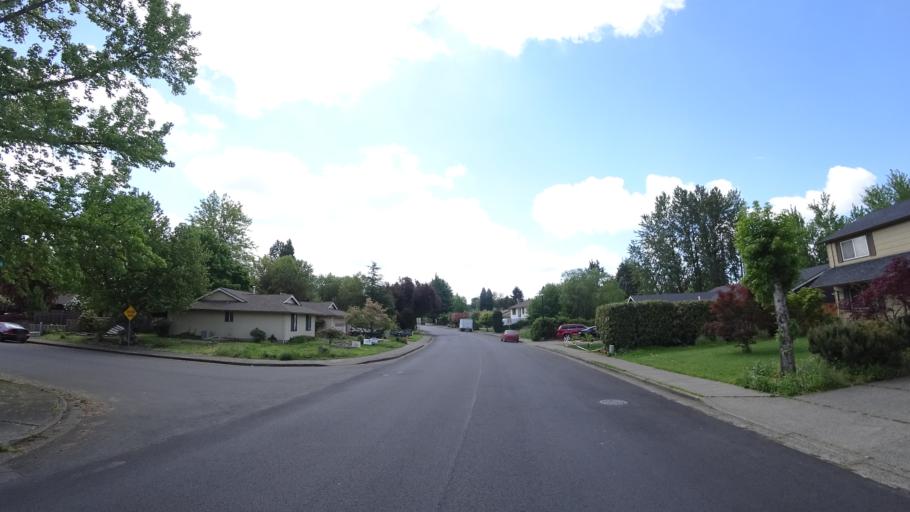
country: US
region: Oregon
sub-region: Washington County
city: Aloha
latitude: 45.5055
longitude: -122.8945
